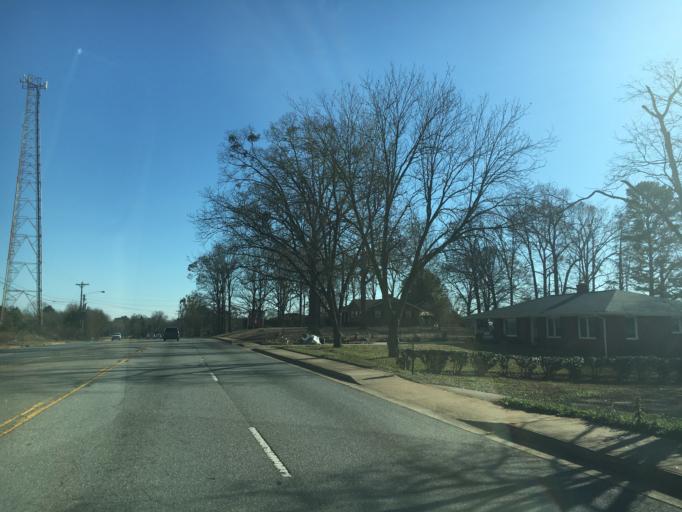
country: US
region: South Carolina
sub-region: Spartanburg County
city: Lyman
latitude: 34.9246
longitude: -82.1191
